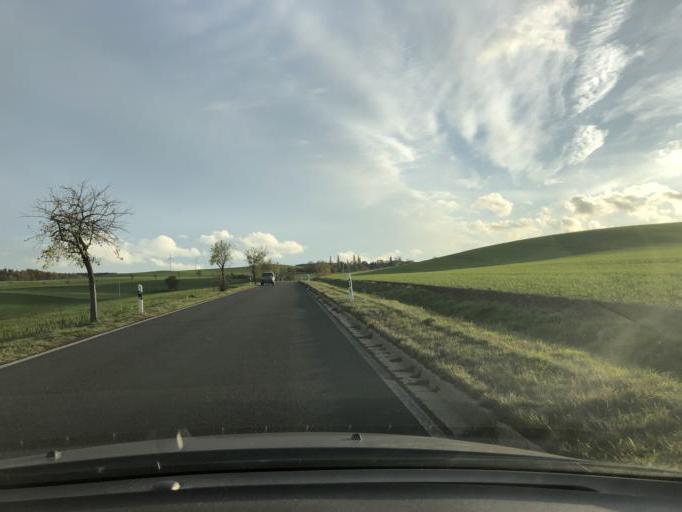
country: DE
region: Thuringia
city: Dreitzsch
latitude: 50.7320
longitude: 11.7998
